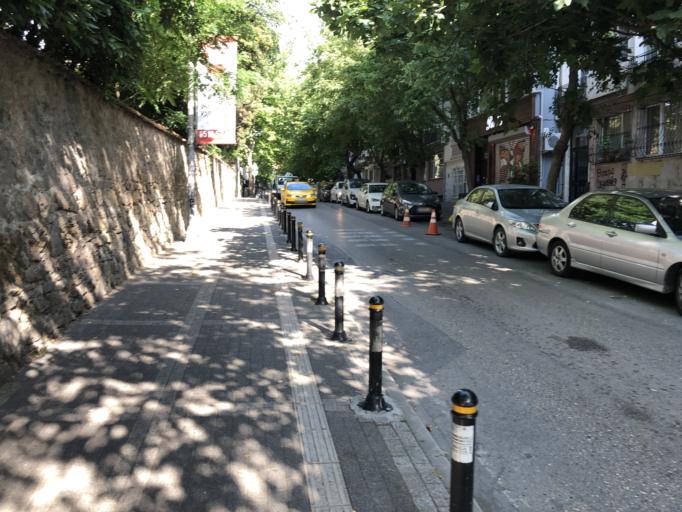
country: TR
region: Istanbul
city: UEskuedar
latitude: 40.9832
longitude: 29.0286
